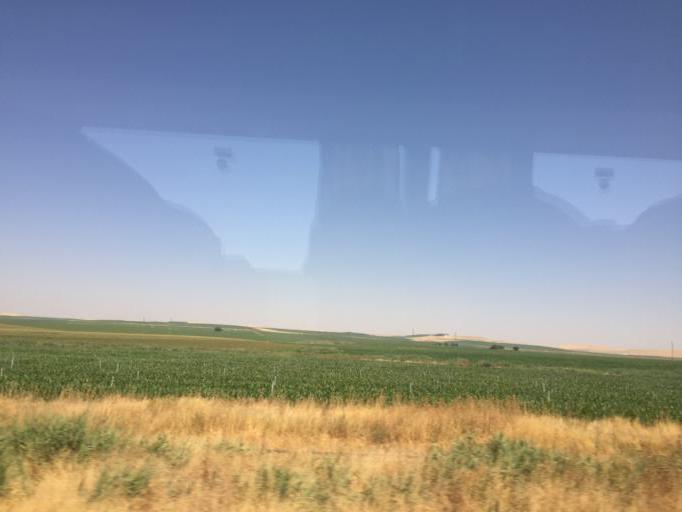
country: TR
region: Diyarbakir
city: Tepe
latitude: 37.8508
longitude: 40.7674
